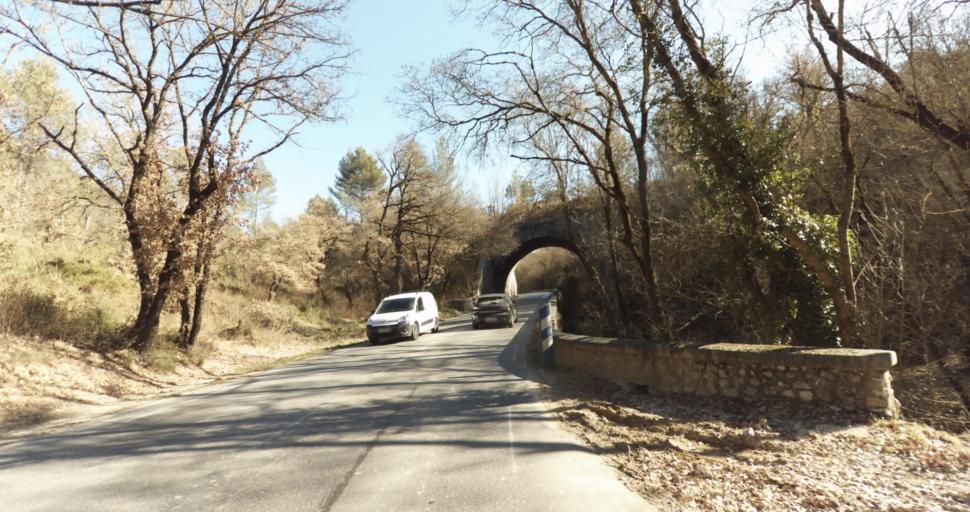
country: FR
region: Provence-Alpes-Cote d'Azur
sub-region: Departement des Bouches-du-Rhone
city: Peypin
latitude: 43.3969
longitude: 5.5745
